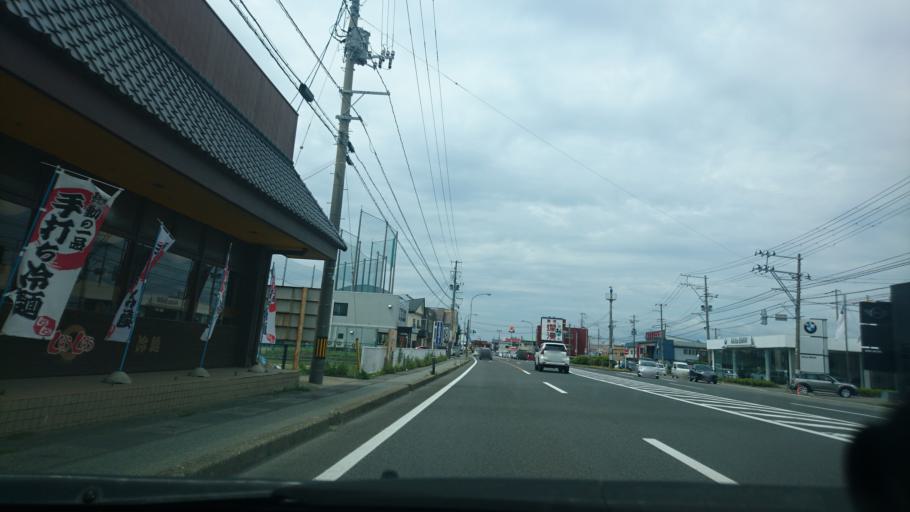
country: JP
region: Akita
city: Akita
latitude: 39.6889
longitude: 140.1238
